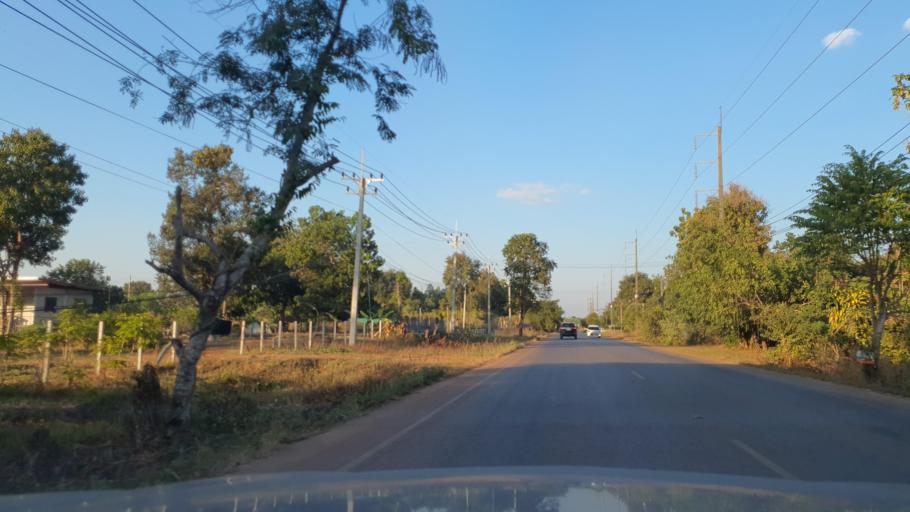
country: TH
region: Nakhon Phanom
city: Si Songkhram
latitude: 17.6019
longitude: 104.2393
